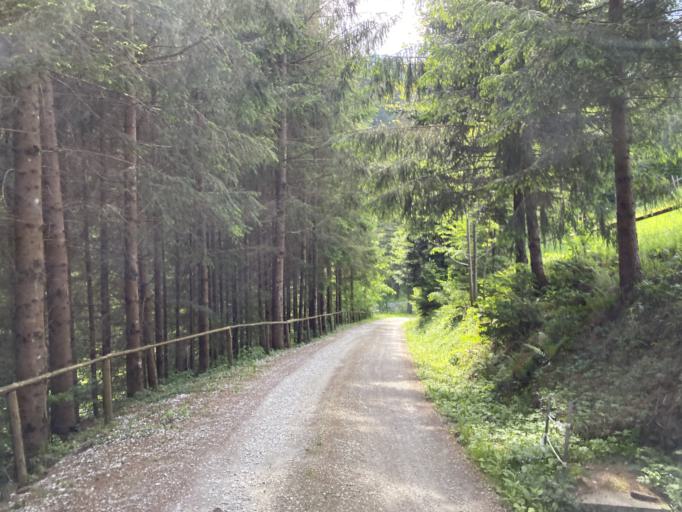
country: AT
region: Styria
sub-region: Politischer Bezirk Weiz
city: Koglhof
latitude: 47.3119
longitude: 15.6536
